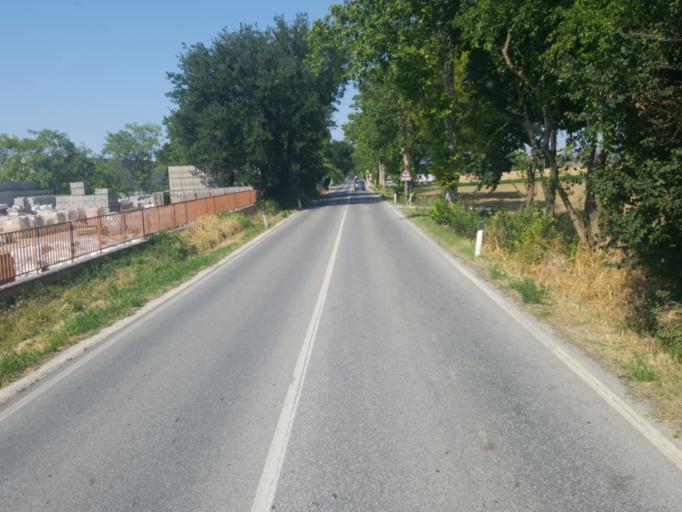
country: IT
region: The Marches
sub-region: Provincia di Ancona
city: Monsano
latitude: 43.5605
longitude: 13.2894
